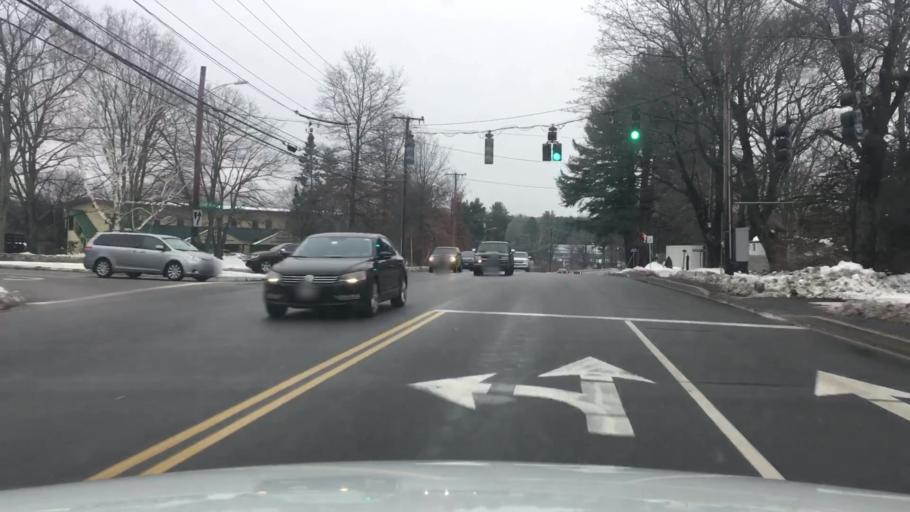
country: US
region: Maine
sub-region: Cumberland County
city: South Portland Gardens
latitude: 43.6115
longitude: -70.3130
